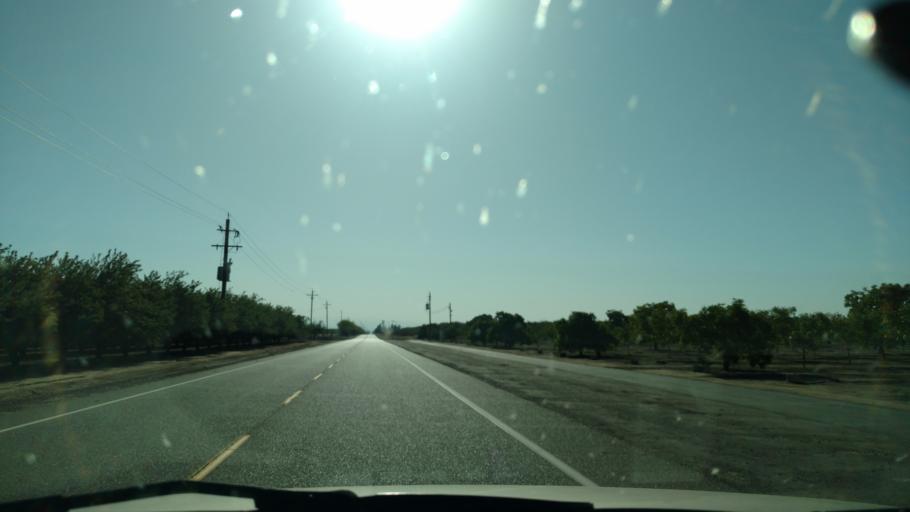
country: US
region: California
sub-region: Madera County
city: Fairmead
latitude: 37.0982
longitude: -120.1686
